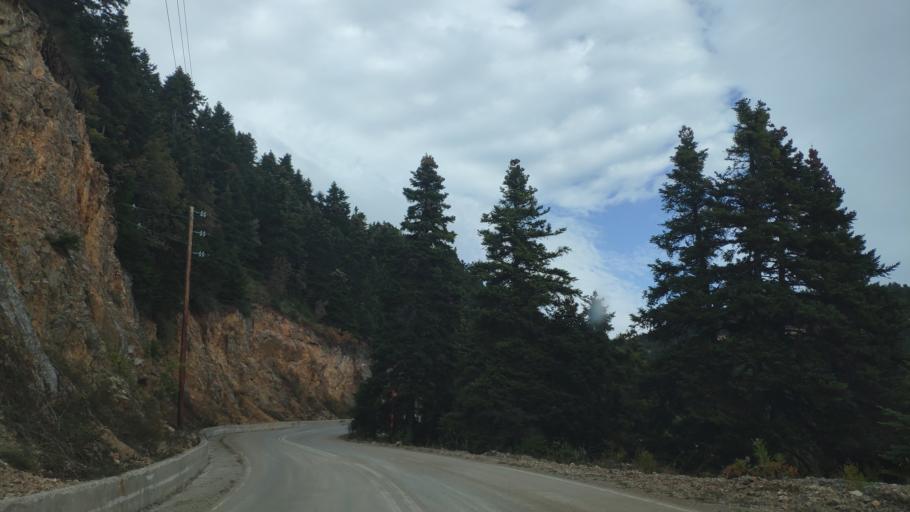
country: GR
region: Central Greece
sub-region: Nomos Fokidos
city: Amfissa
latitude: 38.6971
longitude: 22.3173
